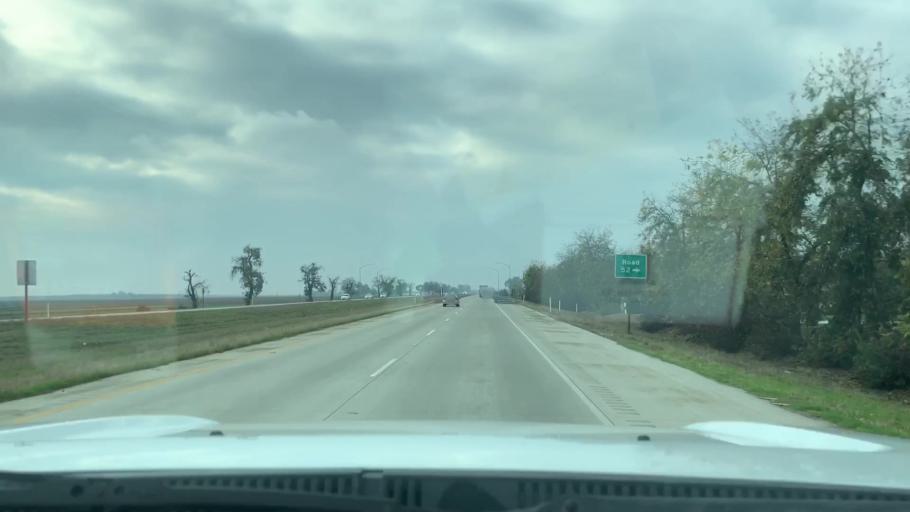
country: US
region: California
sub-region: Tulare County
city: Goshen
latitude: 36.3278
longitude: -119.4542
